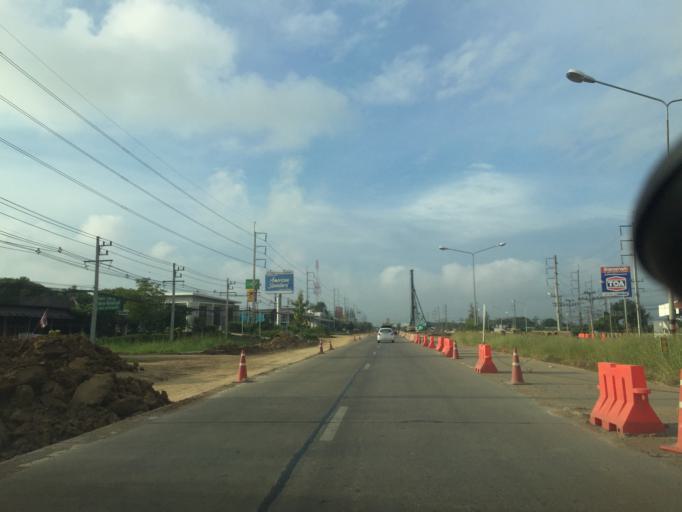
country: TH
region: Lamphun
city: Lamphun
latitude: 18.6165
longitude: 99.0459
